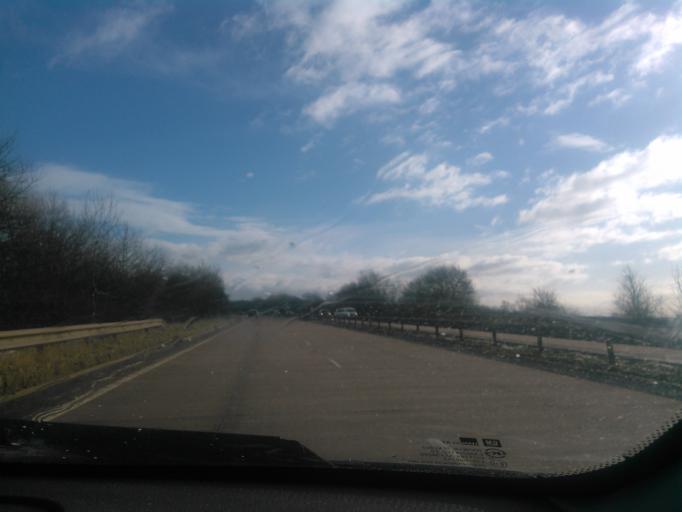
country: GB
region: England
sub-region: Staffordshire
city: Cheadle
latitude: 52.9448
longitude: -2.0064
